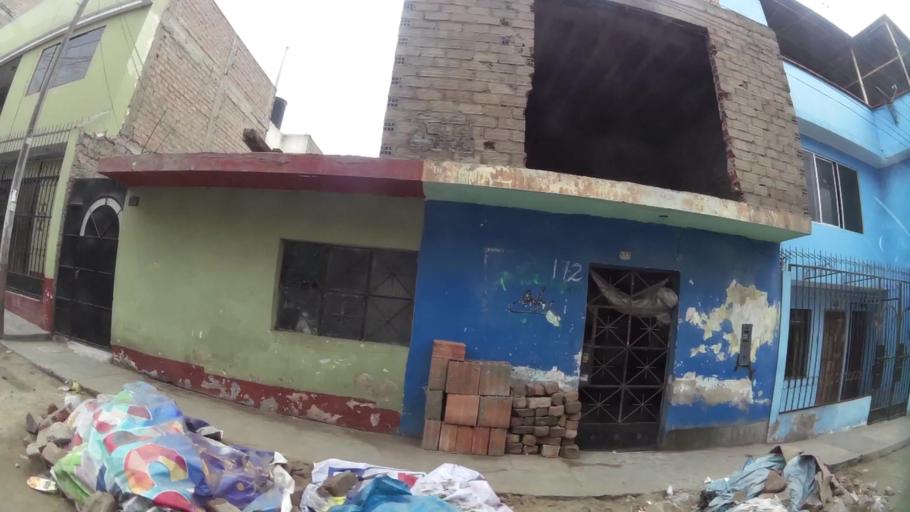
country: PE
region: Lima
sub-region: Lima
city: Surco
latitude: -12.1558
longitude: -76.9575
